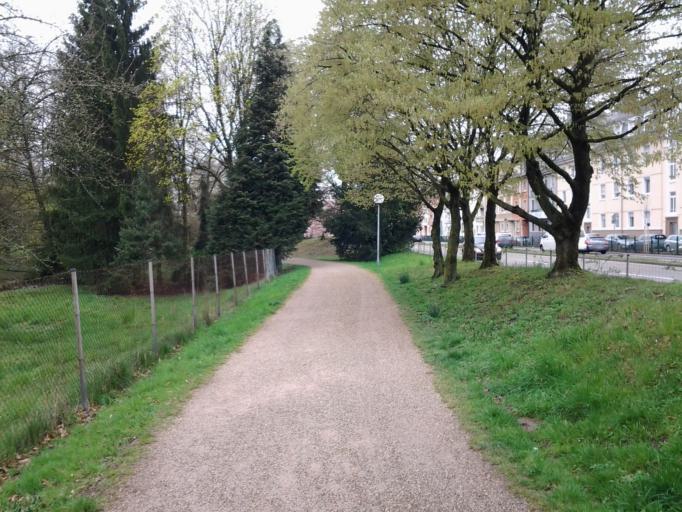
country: DE
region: Baden-Wuerttemberg
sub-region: Karlsruhe Region
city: Baden-Baden
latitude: 48.7737
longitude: 8.2216
